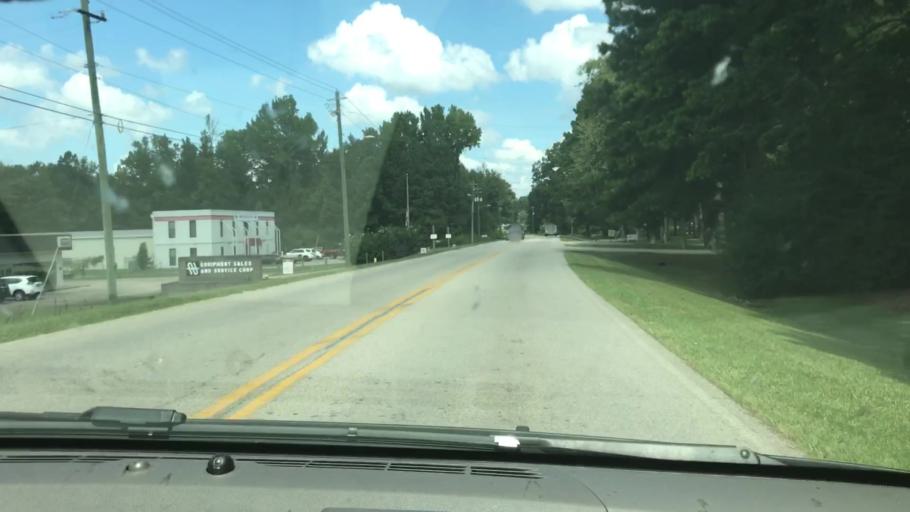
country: US
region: Georgia
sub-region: Troup County
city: La Grange
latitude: 33.0146
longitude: -85.0662
